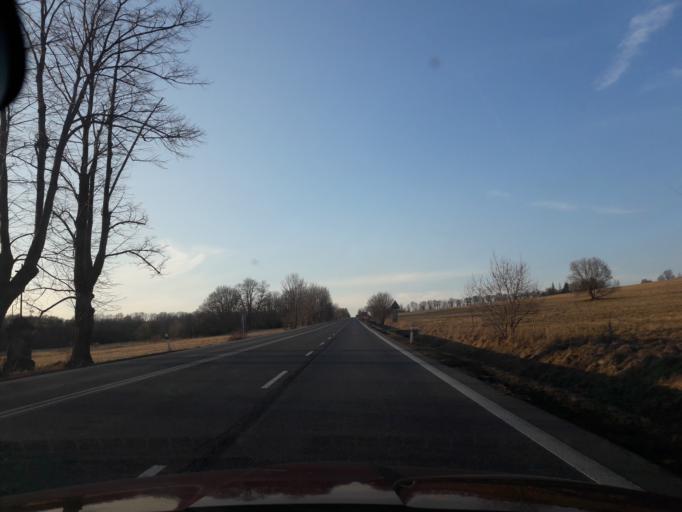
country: CZ
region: Ustecky
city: Dolni Podluzi
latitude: 50.8853
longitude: 14.5779
